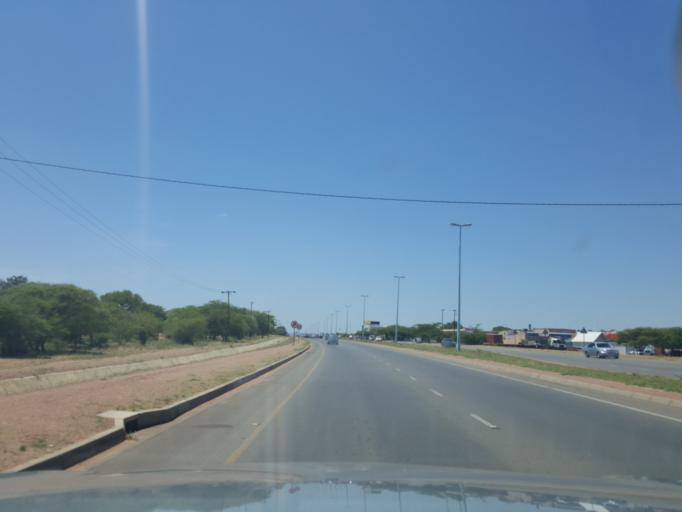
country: BW
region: Kweneng
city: Mogoditshane
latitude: -24.6031
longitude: 25.8555
